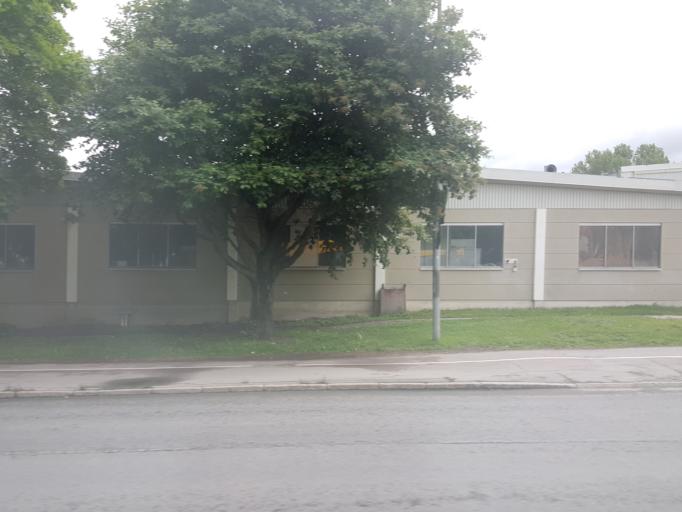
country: SE
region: Uppsala
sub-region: Uppsala Kommun
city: Uppsala
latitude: 59.8536
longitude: 17.6527
